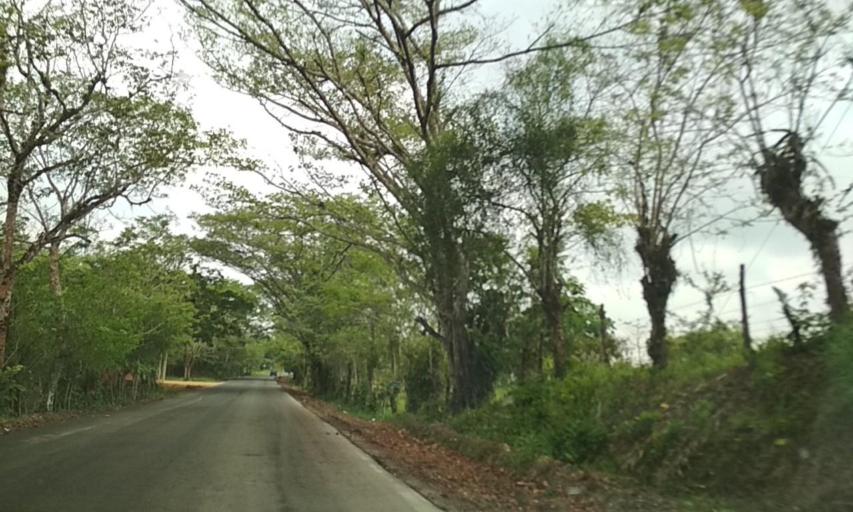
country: MX
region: Tabasco
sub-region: Huimanguillo
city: Francisco Rueda
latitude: 17.6813
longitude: -94.0924
